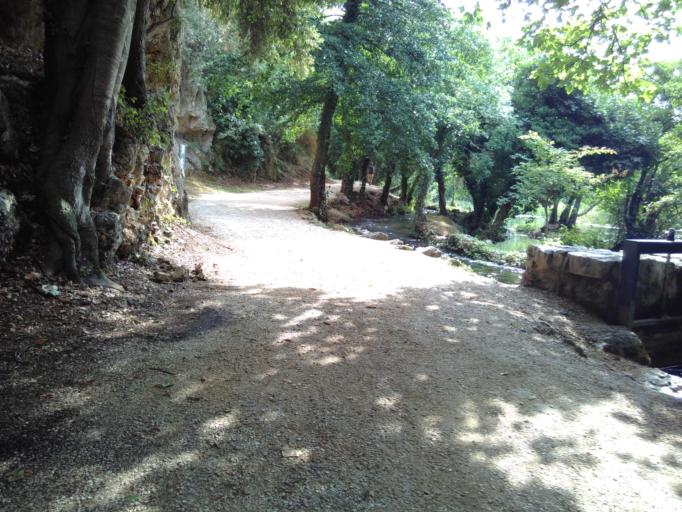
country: HR
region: Sibensko-Kniniska
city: Kistanje
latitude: 43.9074
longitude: 15.9786
